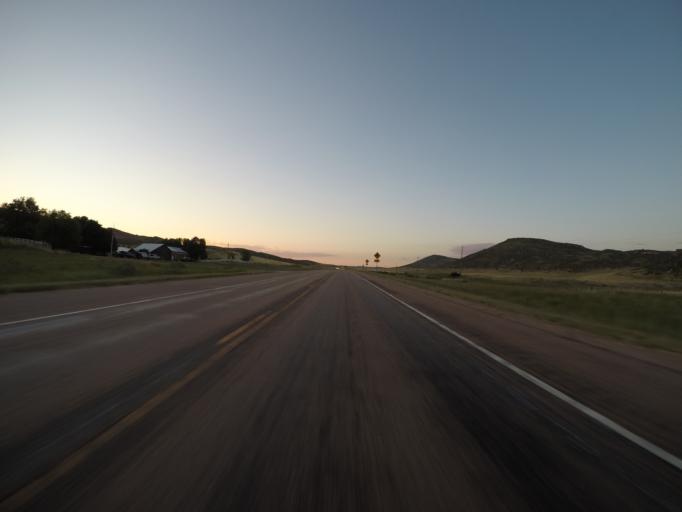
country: US
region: Colorado
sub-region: Larimer County
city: Laporte
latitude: 40.7293
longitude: -105.1714
